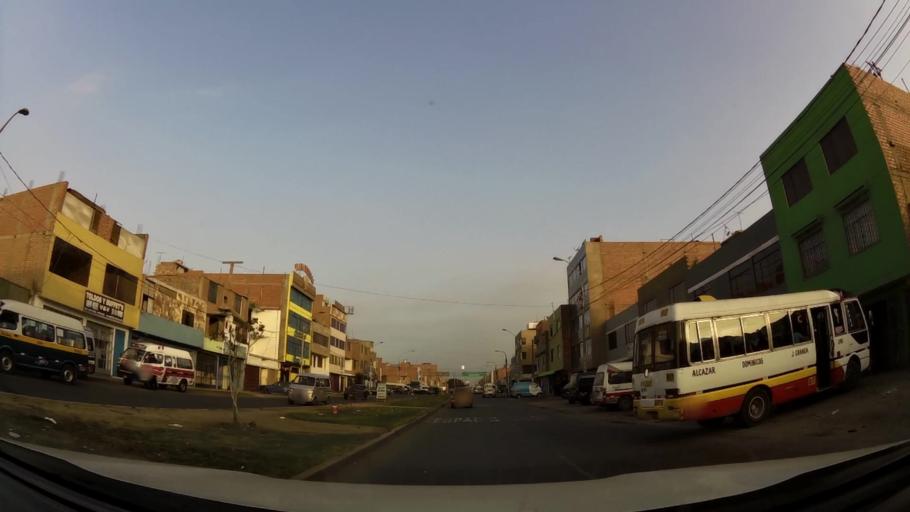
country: PE
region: Callao
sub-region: Callao
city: Callao
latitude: -11.9984
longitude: -77.1077
